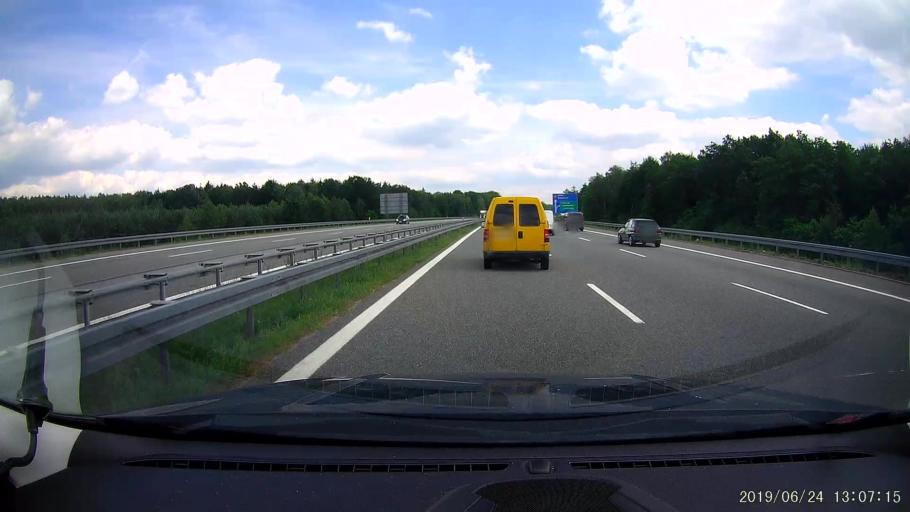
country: PL
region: Silesian Voivodeship
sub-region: Powiat rybnicki
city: Czerwionka-Leszczyny
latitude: 50.1489
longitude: 18.6977
